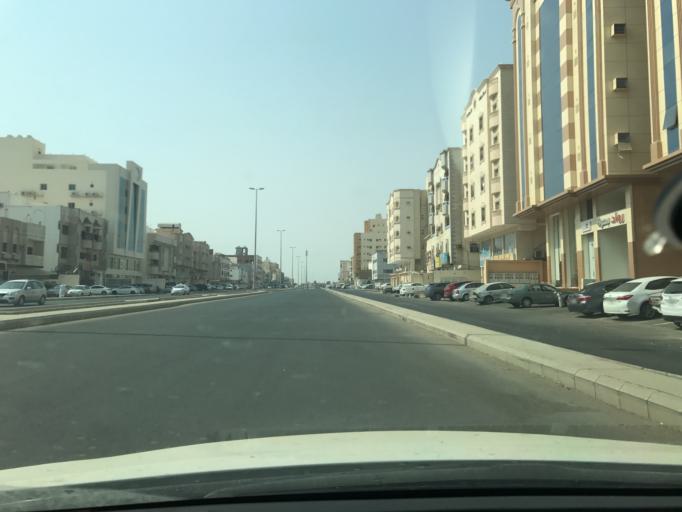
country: SA
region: Makkah
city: Jeddah
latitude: 21.6240
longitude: 39.1689
